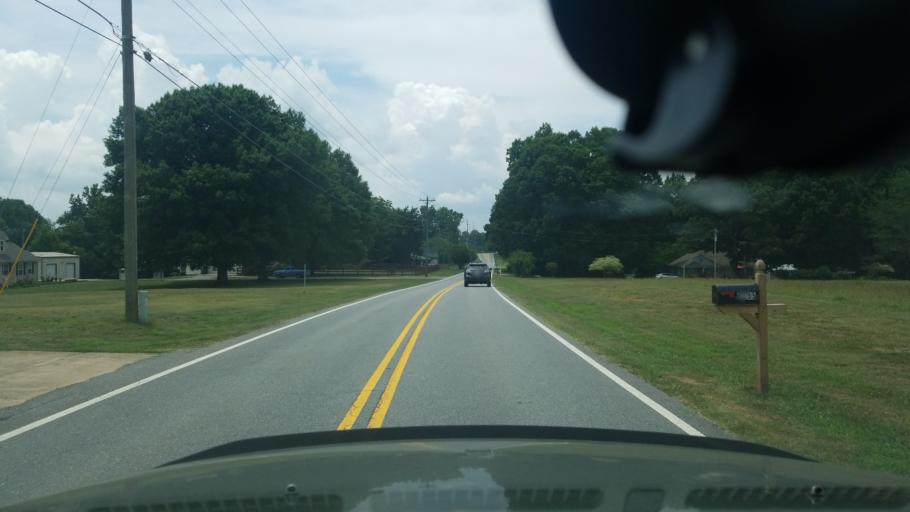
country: US
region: Georgia
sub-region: Fulton County
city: Milton
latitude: 34.1945
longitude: -84.2435
